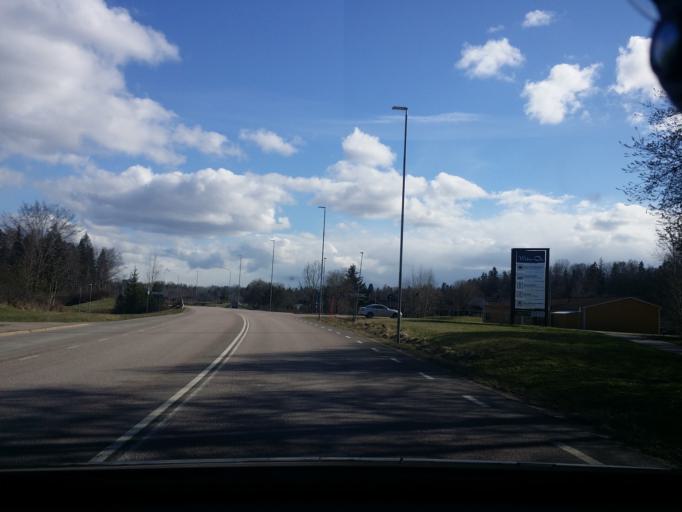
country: SE
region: Vaestmanland
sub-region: Sala Kommun
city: Sala
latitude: 59.9289
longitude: 16.5722
